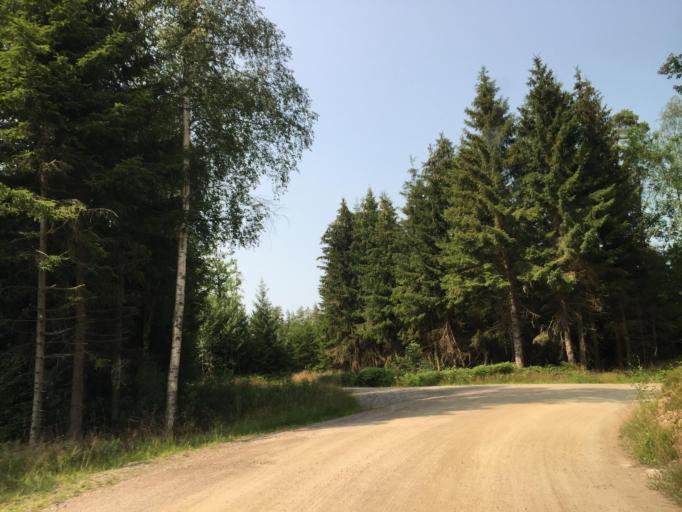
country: SE
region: Vaestra Goetaland
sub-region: Lilla Edets Kommun
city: Lilla Edet
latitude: 58.2337
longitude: 12.1109
